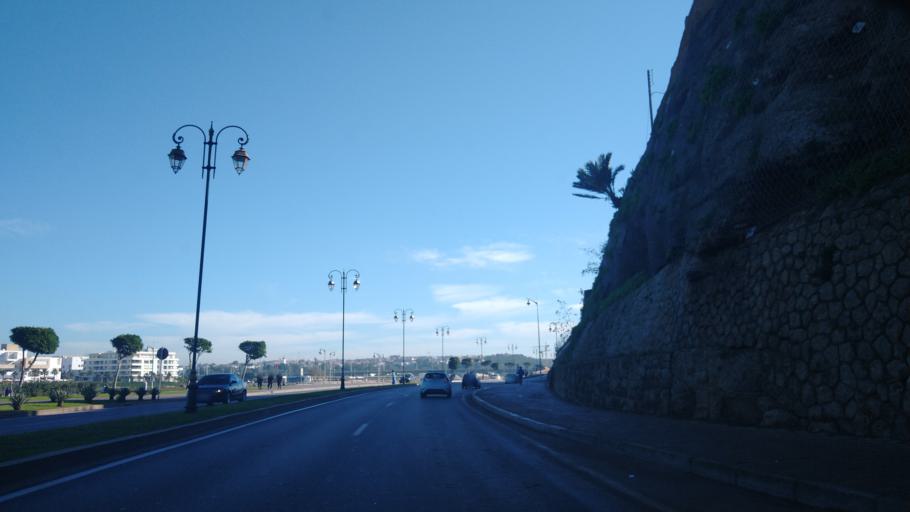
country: MA
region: Rabat-Sale-Zemmour-Zaer
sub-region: Rabat
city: Rabat
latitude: 34.0271
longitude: -6.8286
